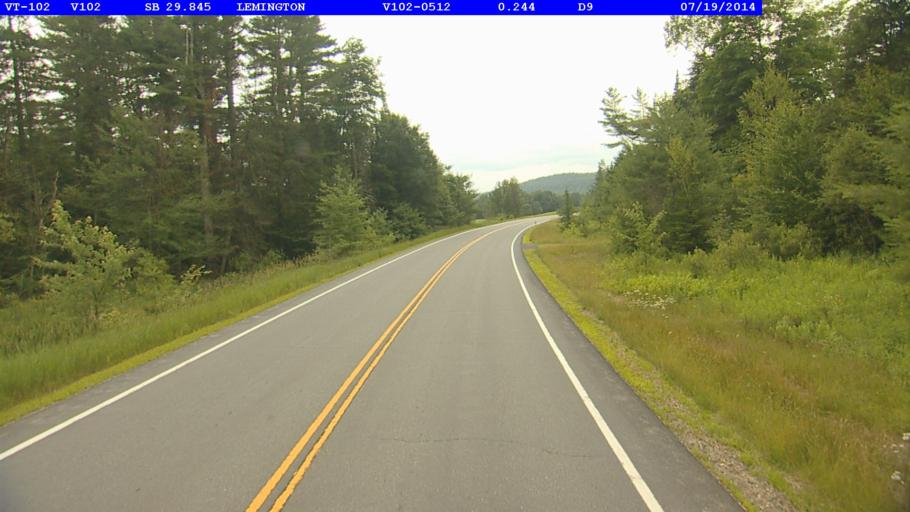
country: US
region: New Hampshire
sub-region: Coos County
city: Colebrook
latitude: 44.8283
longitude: -71.5612
